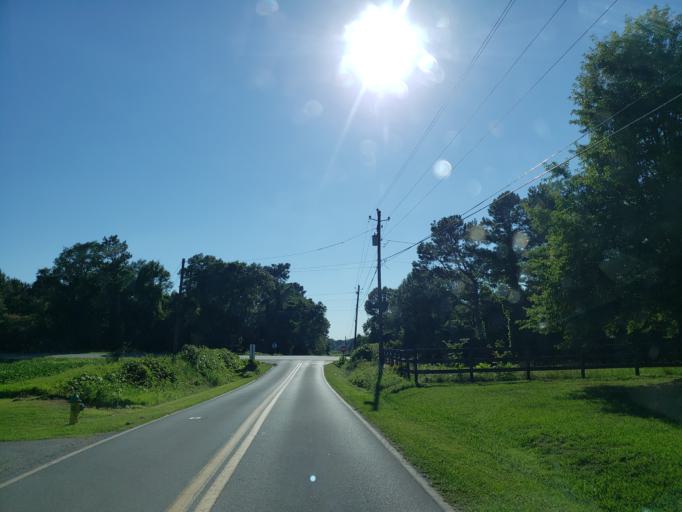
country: US
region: Georgia
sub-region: Bartow County
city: Euharlee
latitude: 34.1085
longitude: -84.9264
